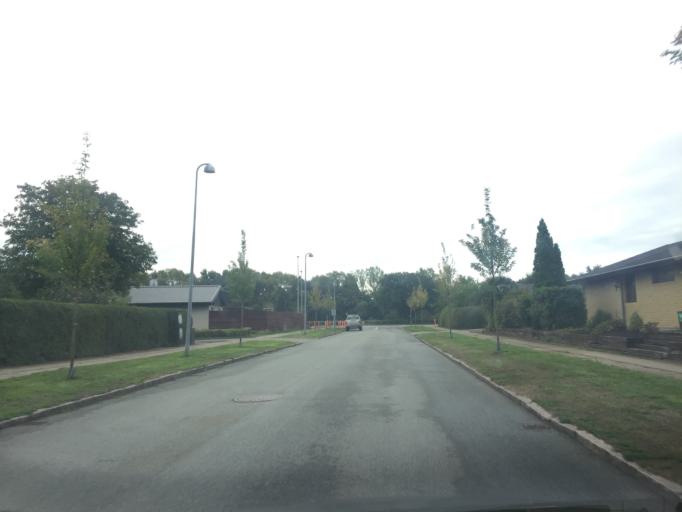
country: DK
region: Capital Region
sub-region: Vallensbaek Kommune
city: Vallensbaek
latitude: 55.6445
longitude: 12.3631
